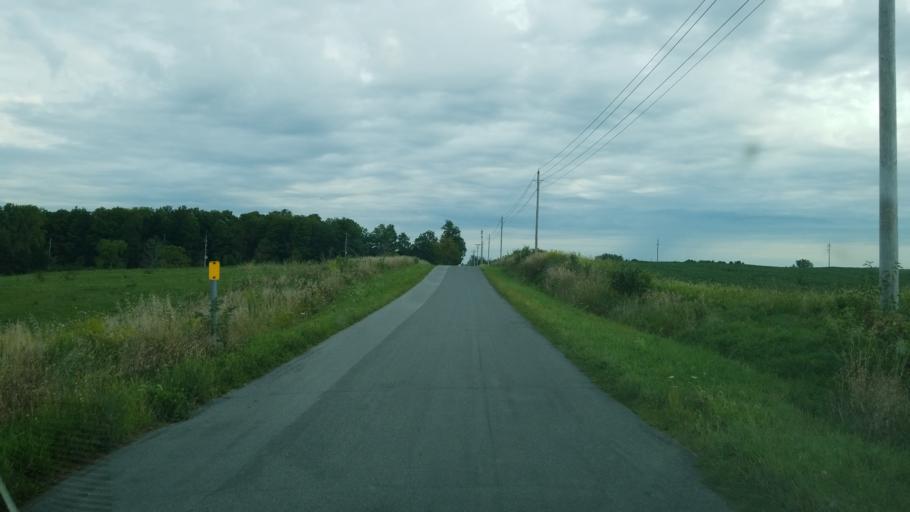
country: US
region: Ohio
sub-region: Crawford County
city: Crestline
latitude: 40.8332
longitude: -82.8185
